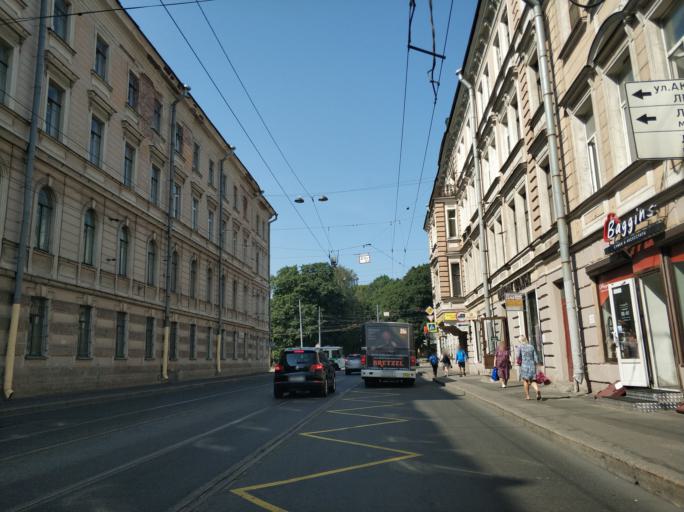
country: RU
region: Leningrad
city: Finlyandskiy
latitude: 59.9557
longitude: 30.3525
